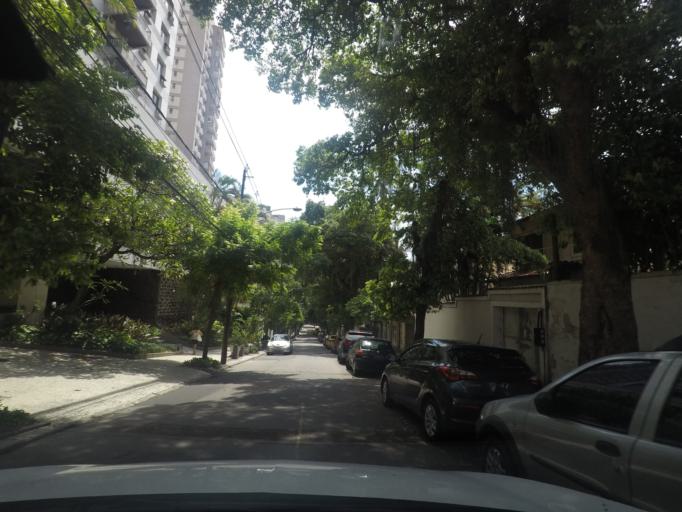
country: BR
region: Rio de Janeiro
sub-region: Rio De Janeiro
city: Rio de Janeiro
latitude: -22.9309
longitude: -43.1892
